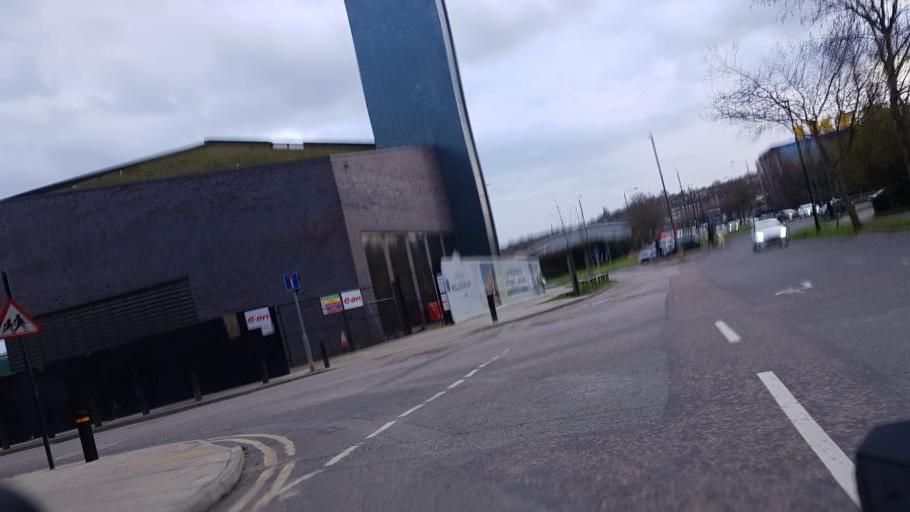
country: GB
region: England
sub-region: Greater London
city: Blackheath
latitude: 51.4915
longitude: 0.0181
